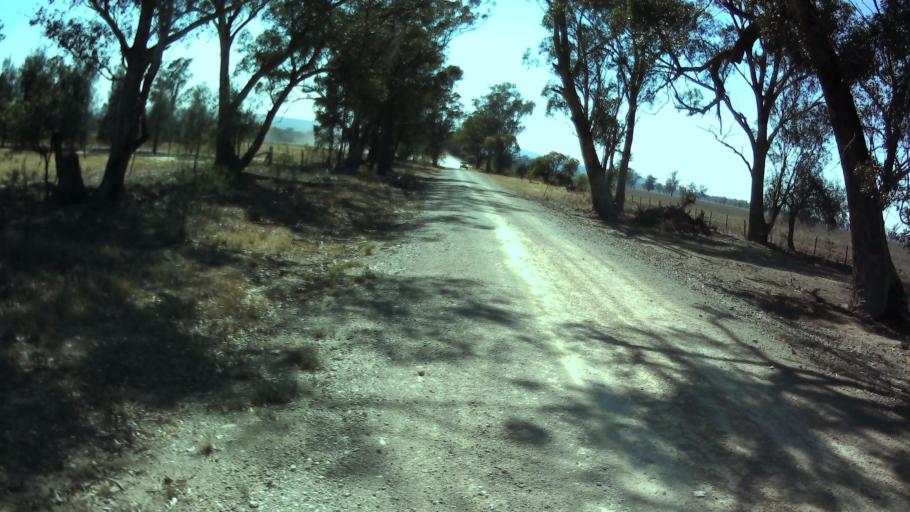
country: AU
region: New South Wales
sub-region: Weddin
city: Grenfell
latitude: -33.9437
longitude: 147.8589
